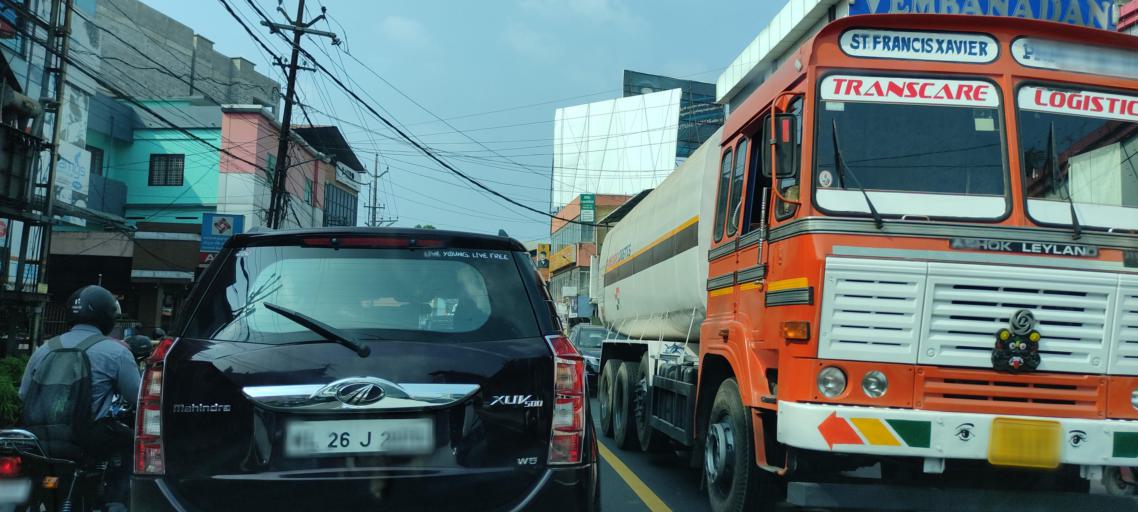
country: IN
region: Kerala
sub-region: Alappuzha
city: Chengannur
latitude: 9.3170
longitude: 76.6163
